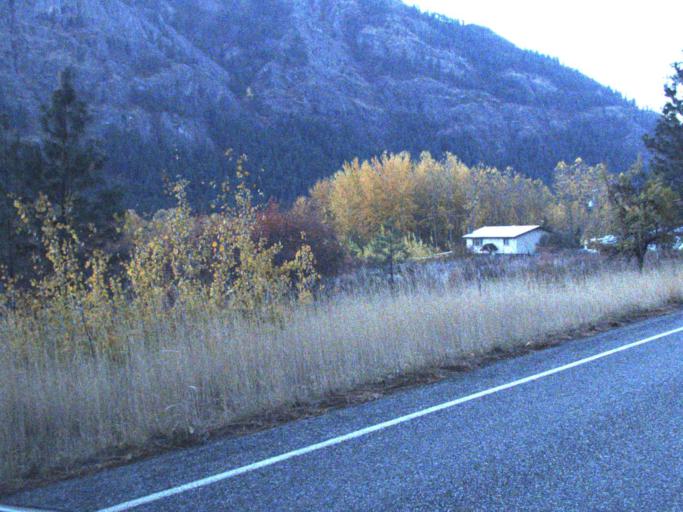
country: US
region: Washington
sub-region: Okanogan County
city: Coulee Dam
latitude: 48.2250
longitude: -118.7052
